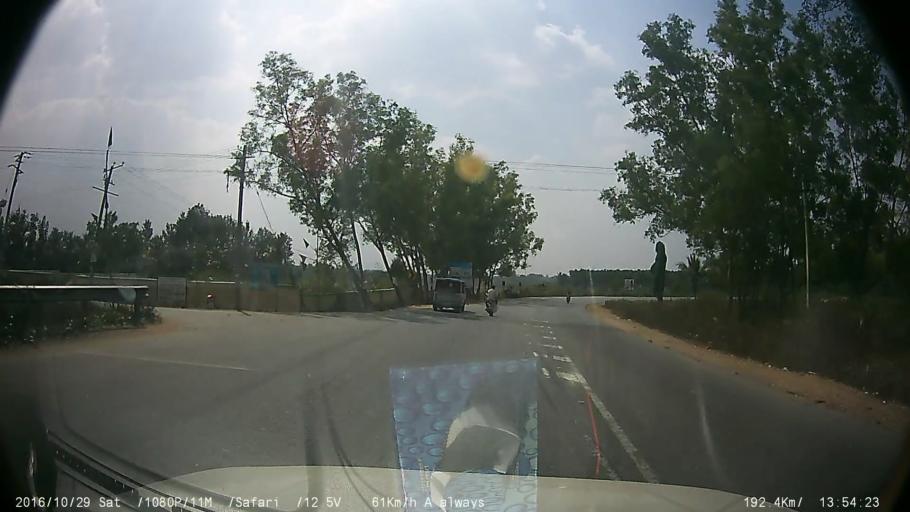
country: IN
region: Karnataka
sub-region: Mysore
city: Piriyapatna
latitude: 12.3374
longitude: 76.1783
